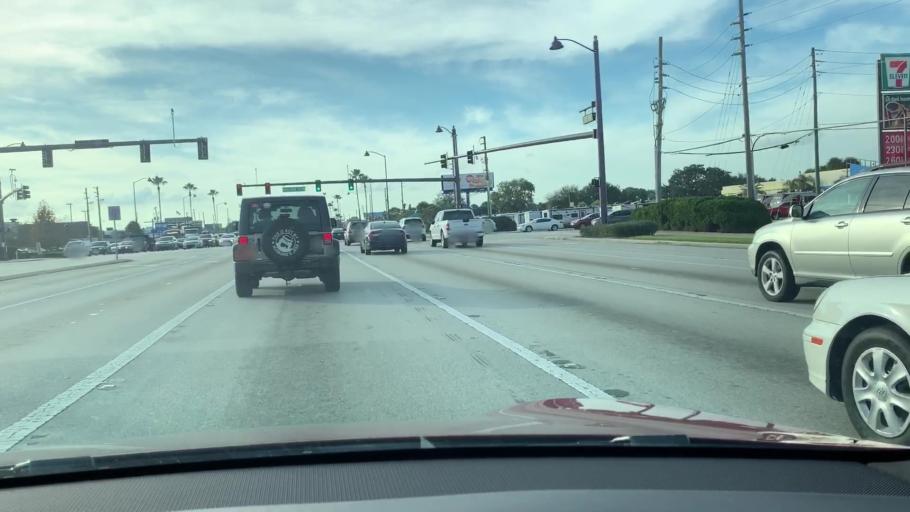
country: US
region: Florida
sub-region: Osceola County
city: Celebration
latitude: 28.3330
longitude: -81.4889
